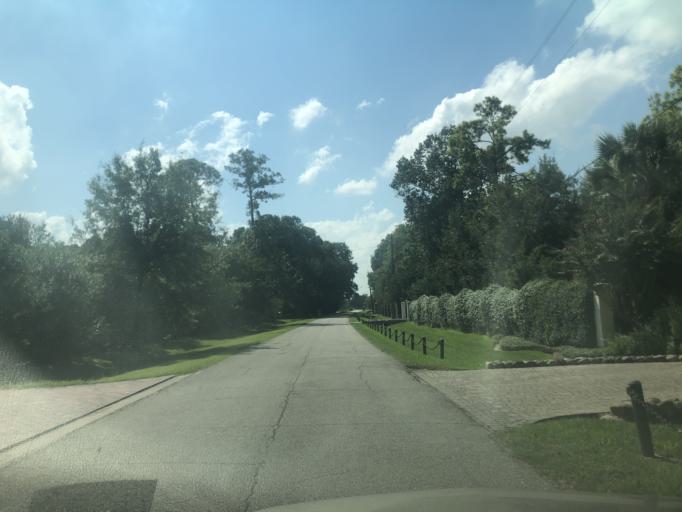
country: US
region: Texas
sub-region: Harris County
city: Bunker Hill Village
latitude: 29.7414
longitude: -95.5457
